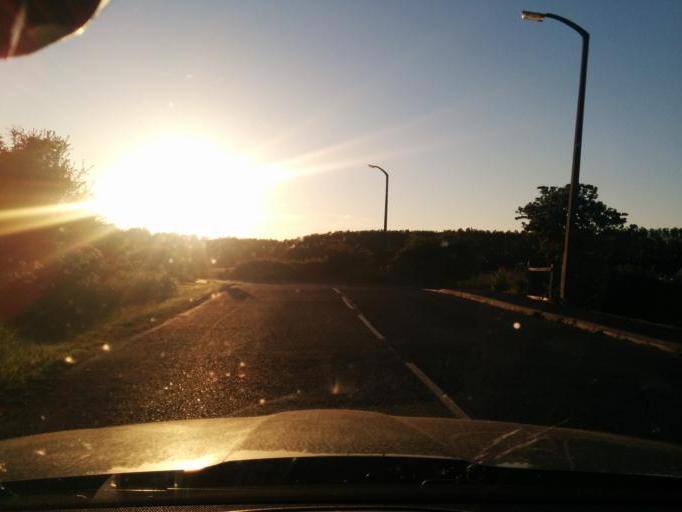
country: GB
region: England
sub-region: Northumberland
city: Cramlington
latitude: 55.1020
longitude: -1.5700
